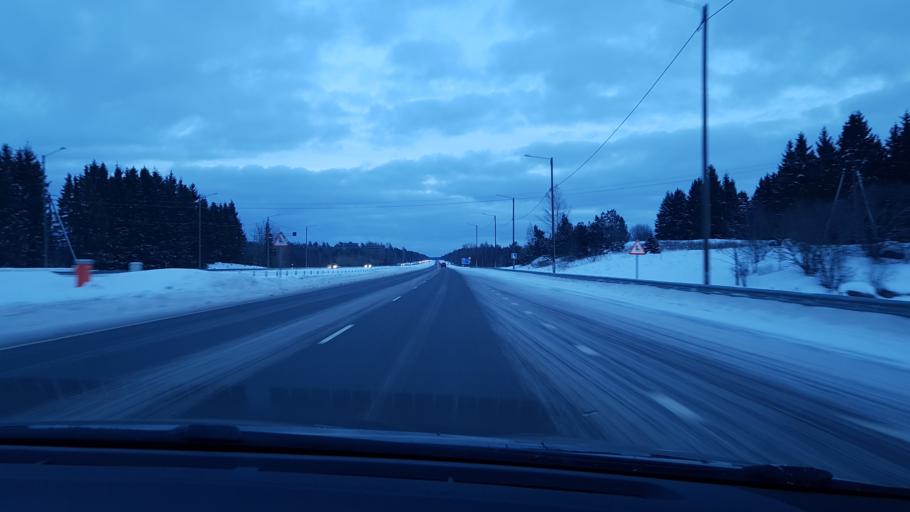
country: EE
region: Harju
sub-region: Kuusalu vald
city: Kuusalu
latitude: 59.4487
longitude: 25.4391
